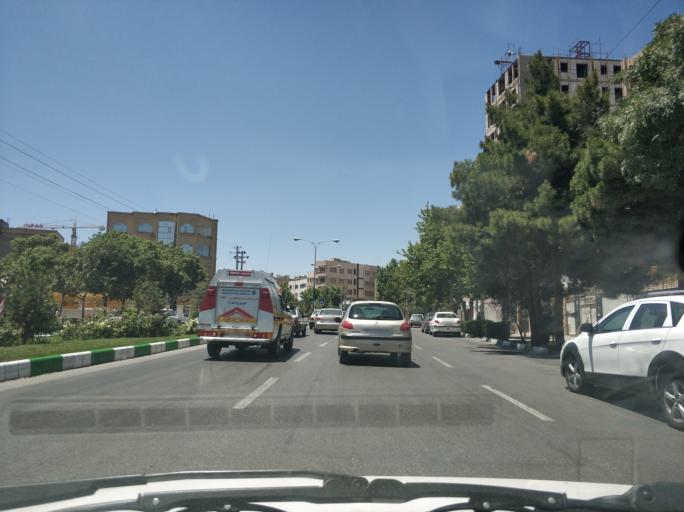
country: IR
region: Razavi Khorasan
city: Mashhad
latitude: 36.3113
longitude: 59.4967
